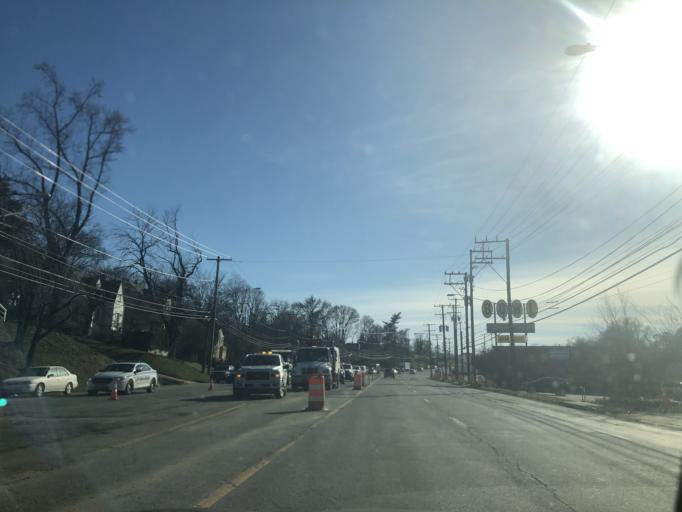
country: US
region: Maryland
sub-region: Prince George's County
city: East Riverdale
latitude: 38.9654
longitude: -76.9189
